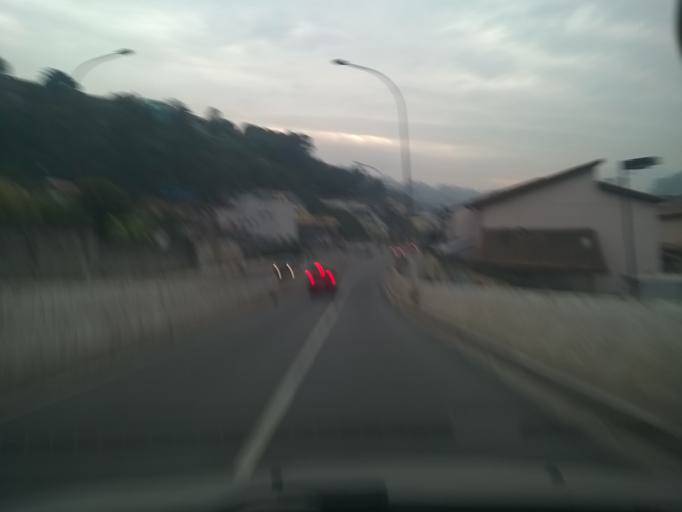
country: BR
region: Sao Paulo
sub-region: Caieiras
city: Caieiras
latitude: -23.4050
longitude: -46.7511
